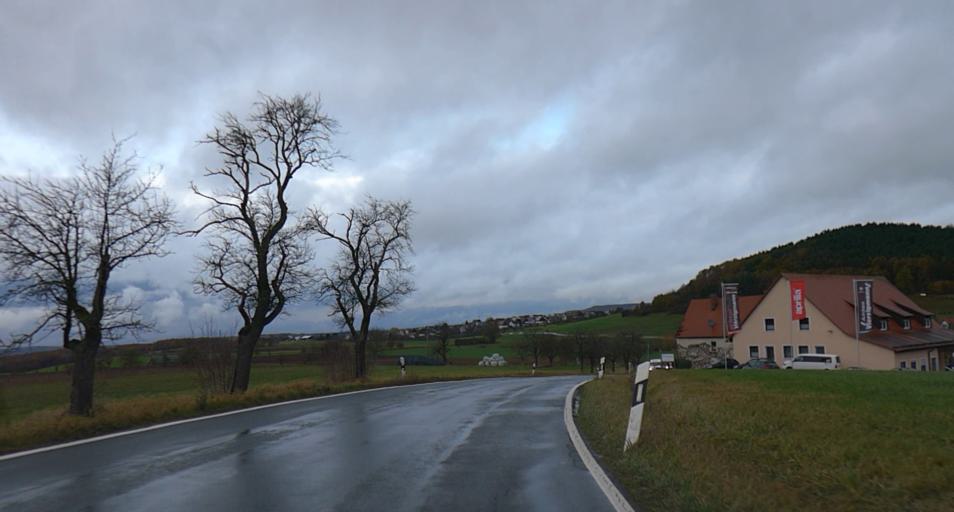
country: DE
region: Bavaria
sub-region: Upper Franconia
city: Leutenbach
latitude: 49.6971
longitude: 11.1626
